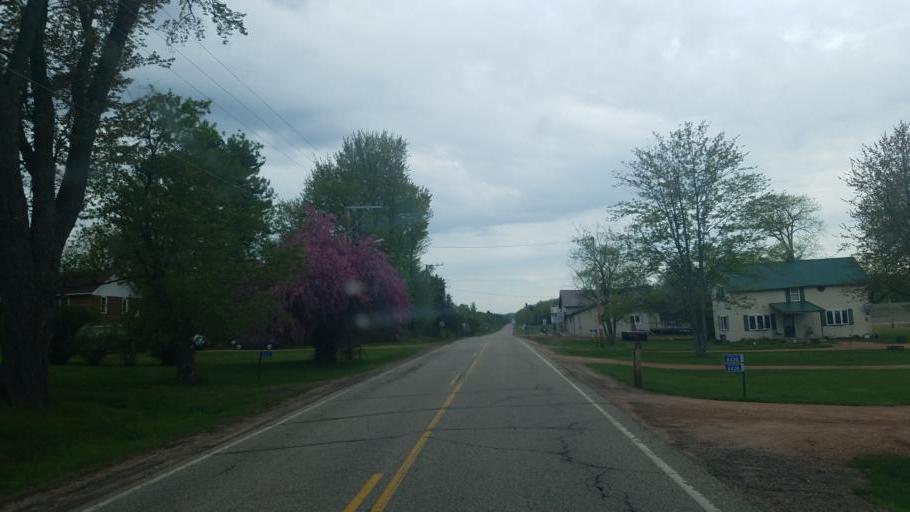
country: US
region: Wisconsin
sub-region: Wood County
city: Marshfield
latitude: 44.5545
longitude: -90.3000
